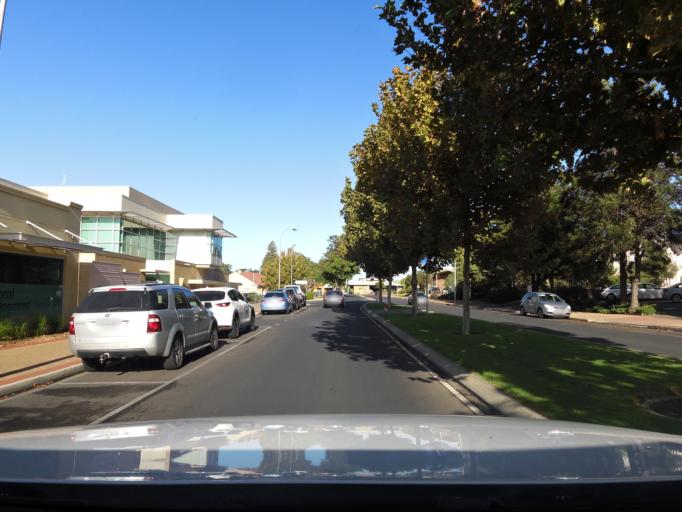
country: AU
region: South Australia
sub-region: Berri and Barmera
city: Berri
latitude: -34.2844
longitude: 140.6033
